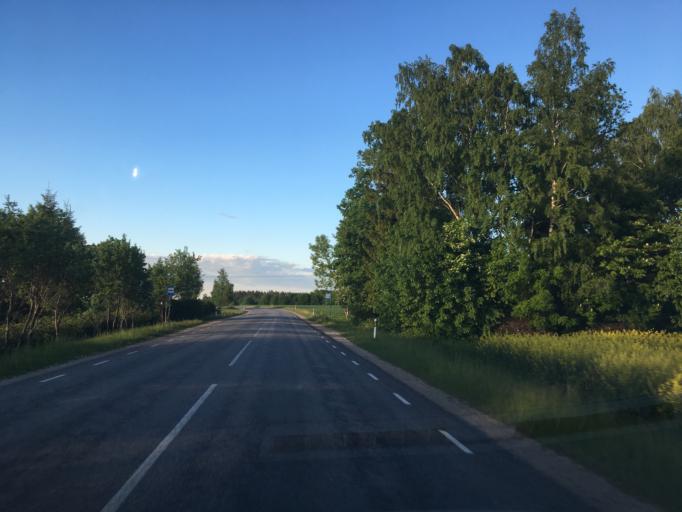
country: EE
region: Tartu
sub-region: Noo vald
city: Noo
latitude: 58.2187
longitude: 26.6235
